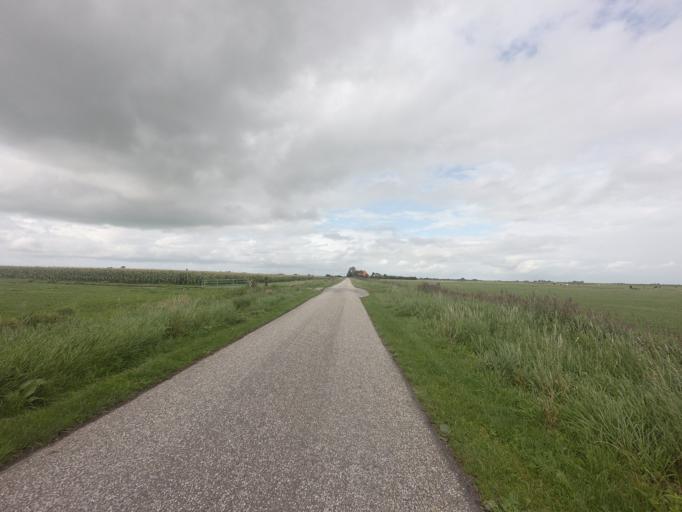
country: NL
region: Friesland
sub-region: Sudwest Fryslan
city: Workum
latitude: 52.9874
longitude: 5.4918
